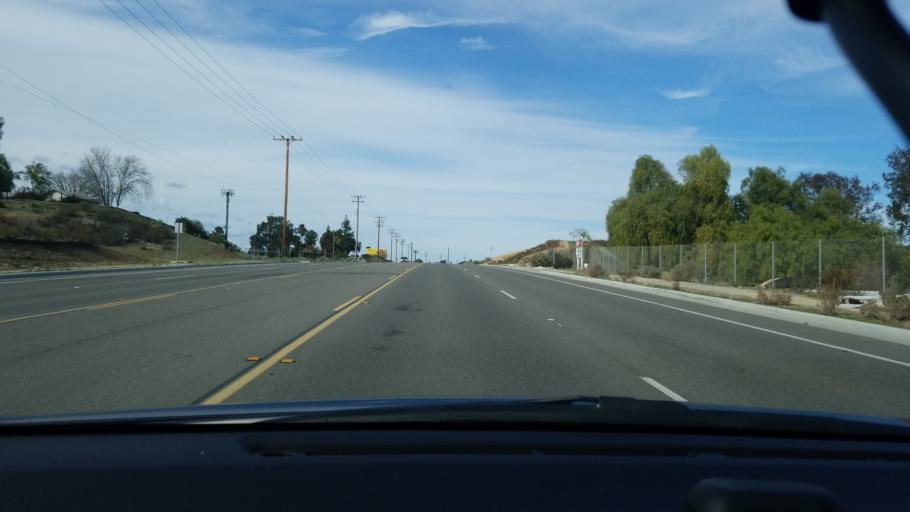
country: US
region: California
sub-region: Riverside County
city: Murrieta Hot Springs
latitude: 33.5440
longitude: -117.1742
